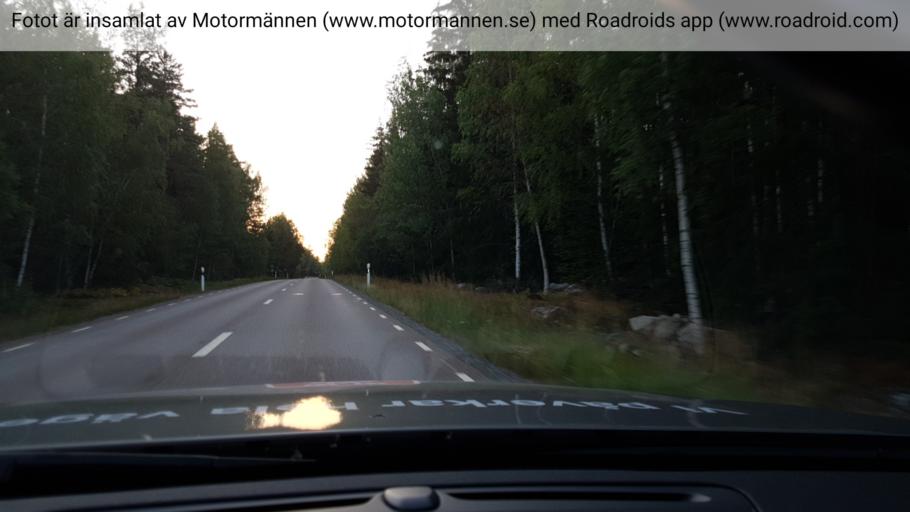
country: SE
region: Uppsala
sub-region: Heby Kommun
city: OEstervala
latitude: 60.0113
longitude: 17.2930
